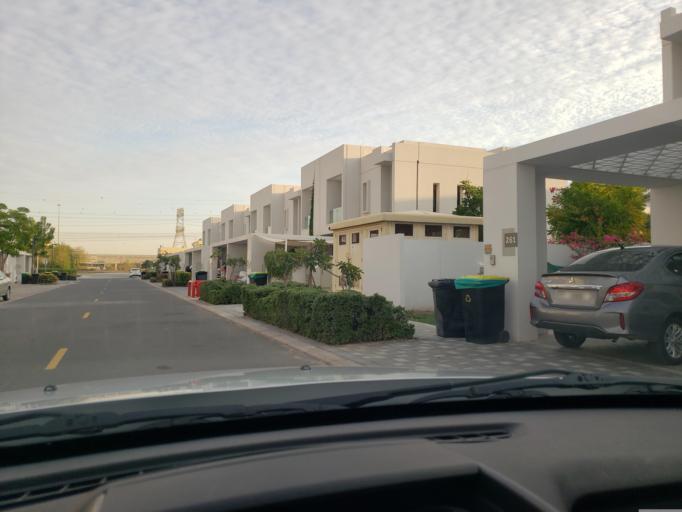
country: AE
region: Dubai
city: Dubai
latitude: 25.0147
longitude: 55.2696
